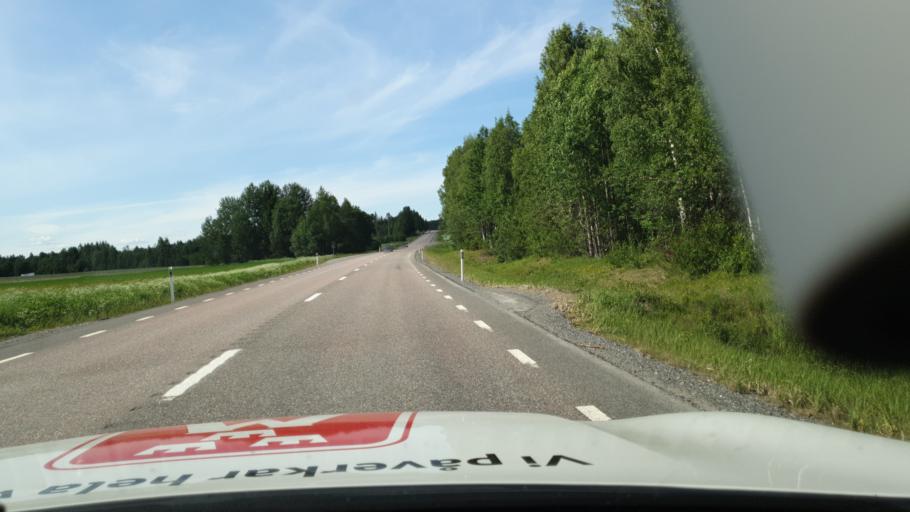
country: SE
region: Vaesterbotten
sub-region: Skelleftea Kommun
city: Viken
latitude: 64.7711
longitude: 20.8444
